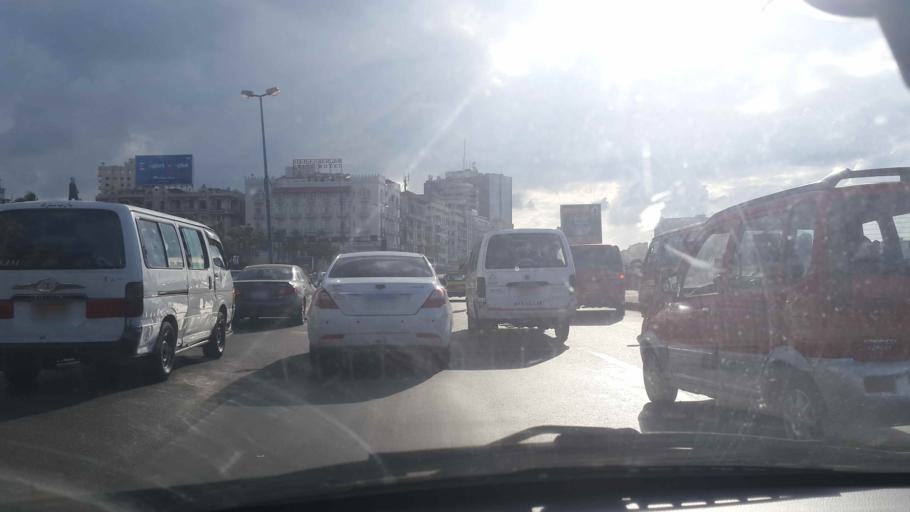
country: EG
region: Alexandria
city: Alexandria
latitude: 31.2020
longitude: 29.9004
